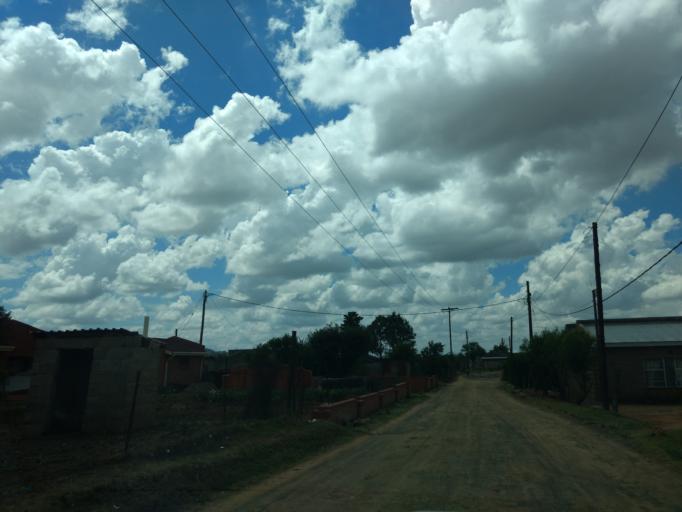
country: LS
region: Maseru
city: Maseru
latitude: -29.3710
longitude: 27.5114
